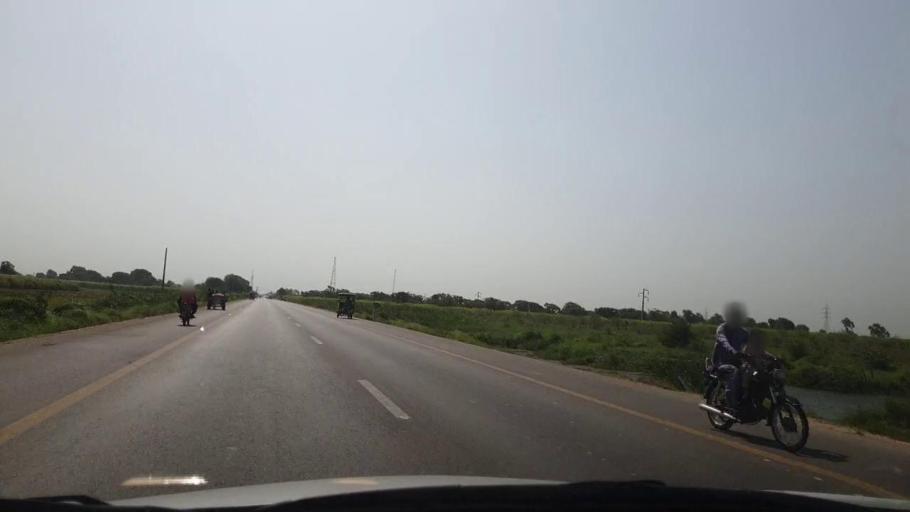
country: PK
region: Sindh
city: Tando Muhammad Khan
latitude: 25.1005
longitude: 68.5903
